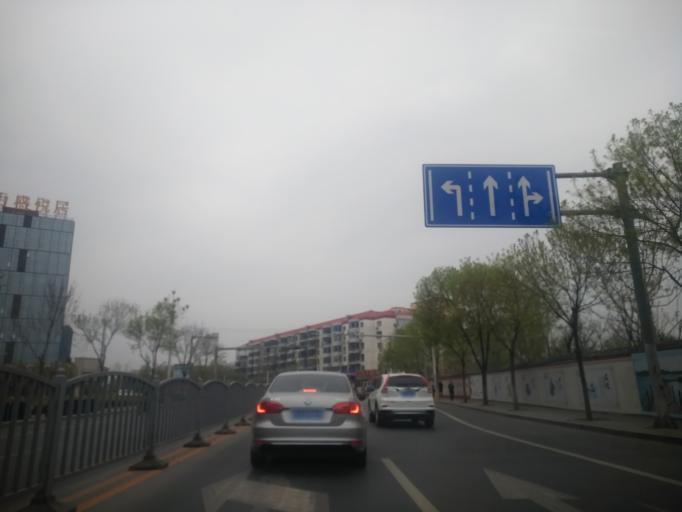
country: CN
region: Beijing
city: Jiugong
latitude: 39.8055
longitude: 116.4511
